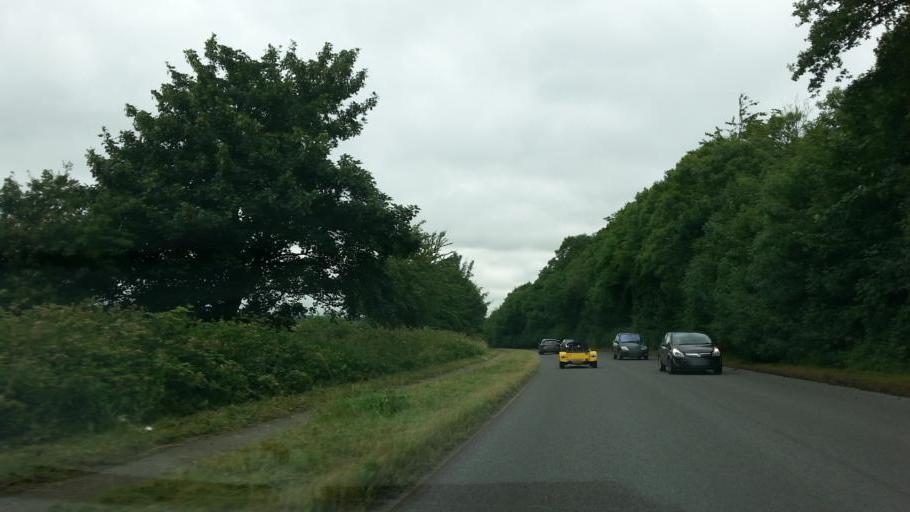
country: GB
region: England
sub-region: Lincolnshire
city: Stamford
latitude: 52.6322
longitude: -0.4938
